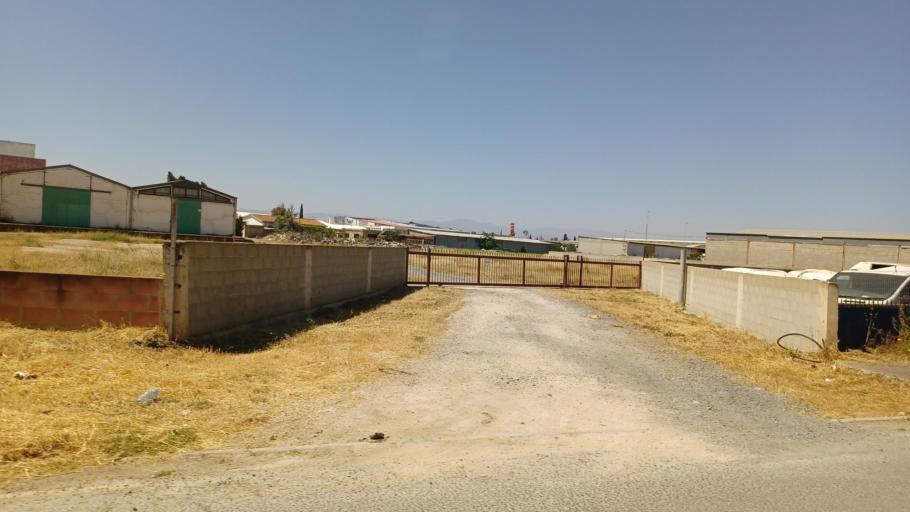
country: CY
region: Lefkosia
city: Kokkinotrimithia
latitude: 35.1528
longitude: 33.2305
